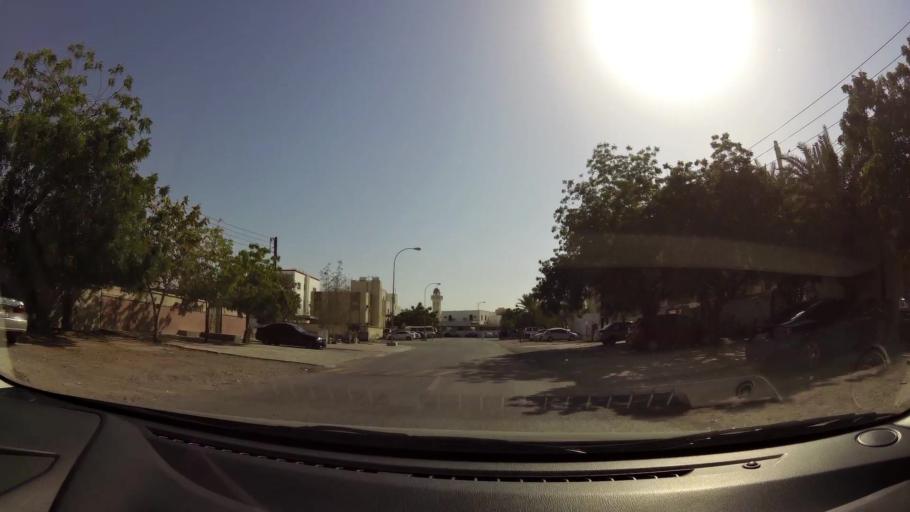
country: OM
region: Muhafazat Masqat
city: As Sib al Jadidah
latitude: 23.6300
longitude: 58.2035
